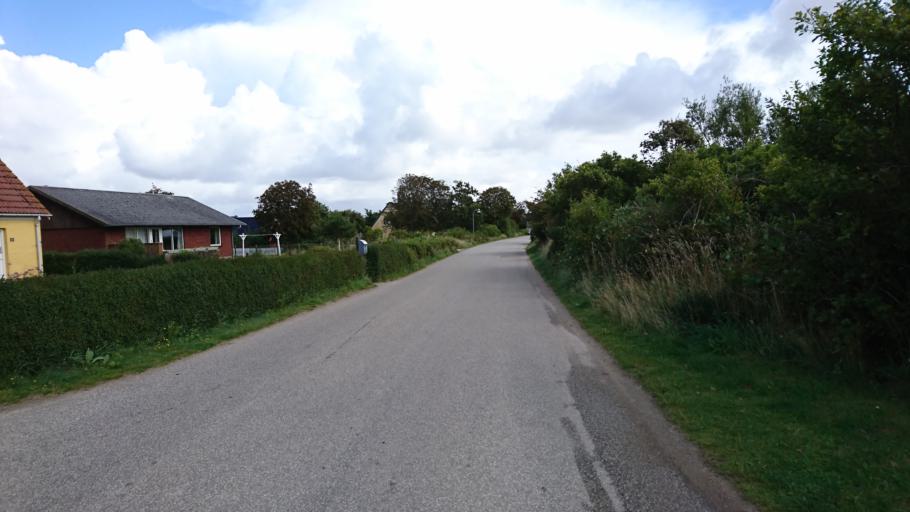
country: DK
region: South Denmark
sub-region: Fano Kommune
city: Nordby
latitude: 55.3490
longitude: 8.4644
